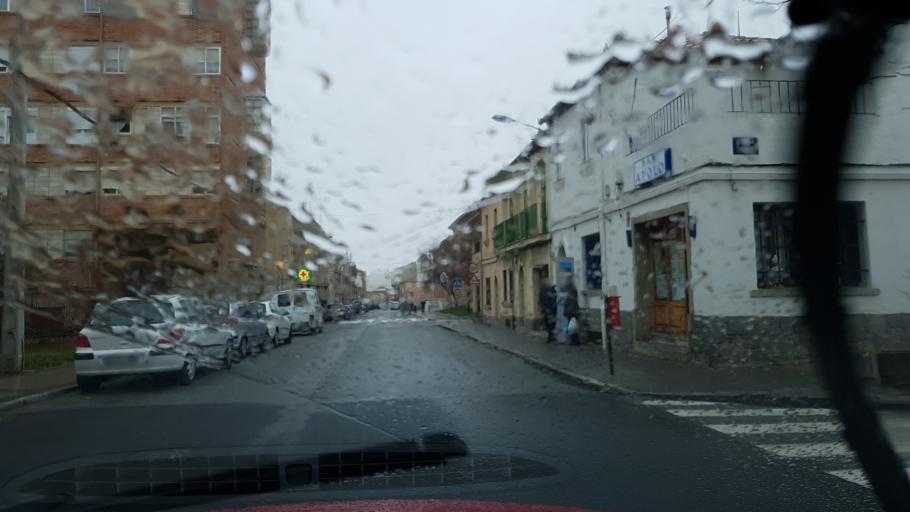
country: ES
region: Castille and Leon
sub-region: Provincia de Segovia
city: Segovia
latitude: 40.9432
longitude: -4.1056
